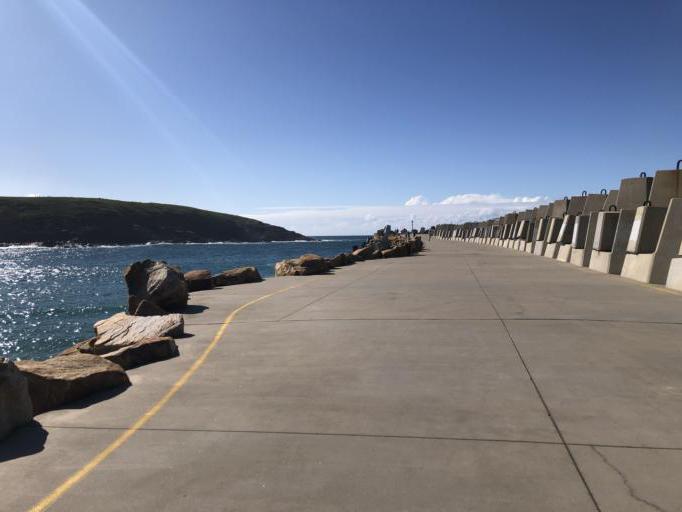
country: AU
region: New South Wales
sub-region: Coffs Harbour
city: Coffs Harbour
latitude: -30.3105
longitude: 153.1517
